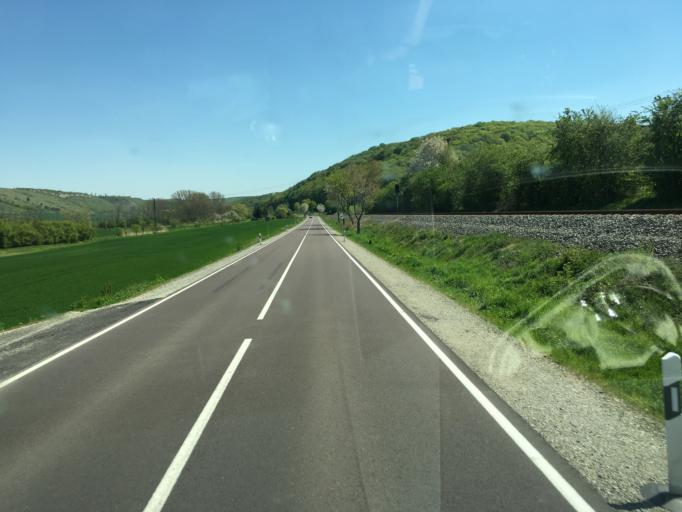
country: DE
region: Saxony-Anhalt
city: Laucha
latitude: 51.2176
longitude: 11.6963
